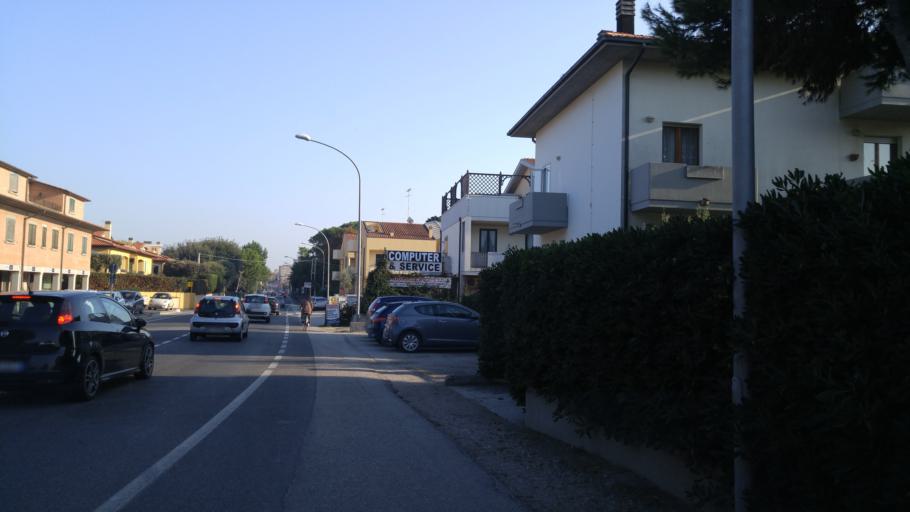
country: IT
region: The Marches
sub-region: Provincia di Pesaro e Urbino
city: Fano
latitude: 43.8505
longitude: 13.0068
